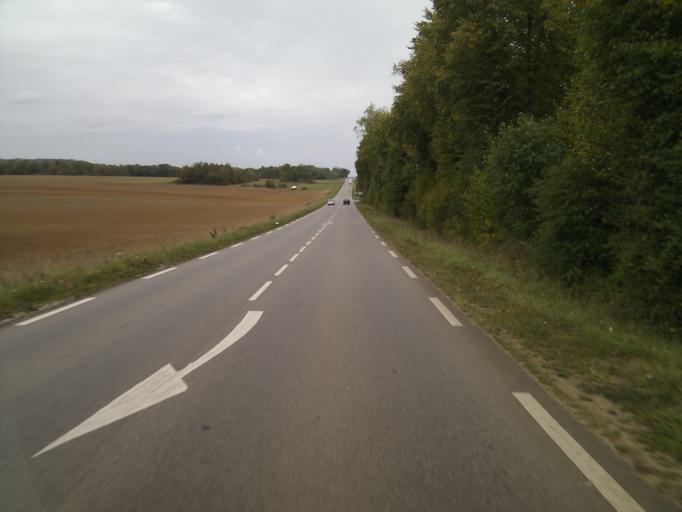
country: FR
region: Lorraine
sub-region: Departement des Vosges
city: Neufchateau
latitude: 48.3882
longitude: 5.7209
